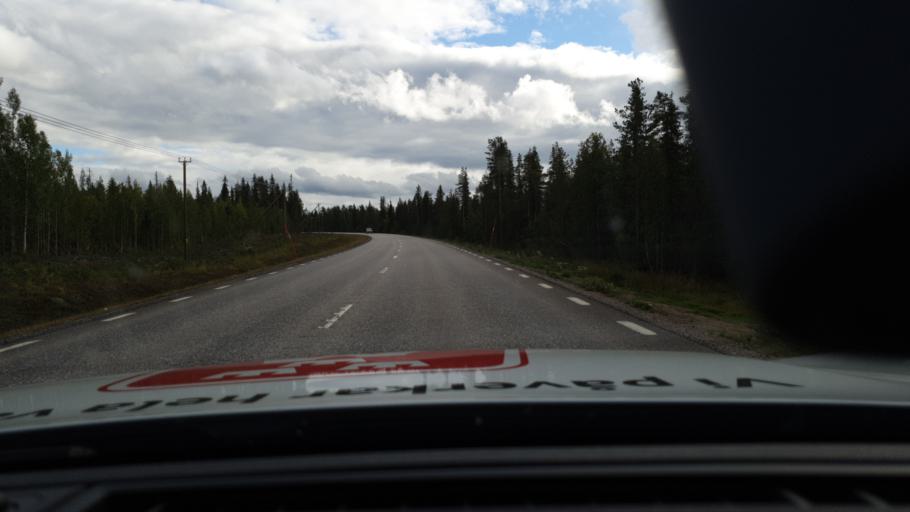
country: SE
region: Norrbotten
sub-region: Gallivare Kommun
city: Gaellivare
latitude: 67.0241
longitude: 21.2564
